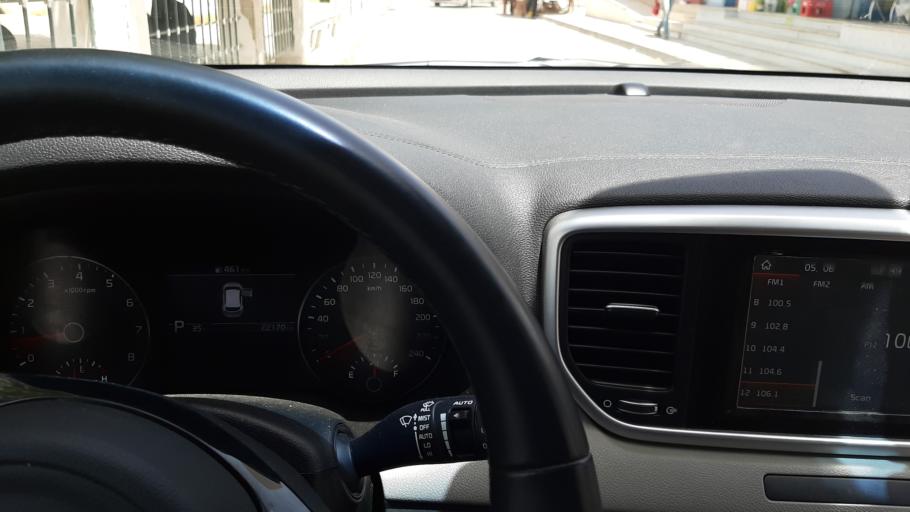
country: TN
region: Qabis
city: Gabes
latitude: 33.6177
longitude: 10.2892
